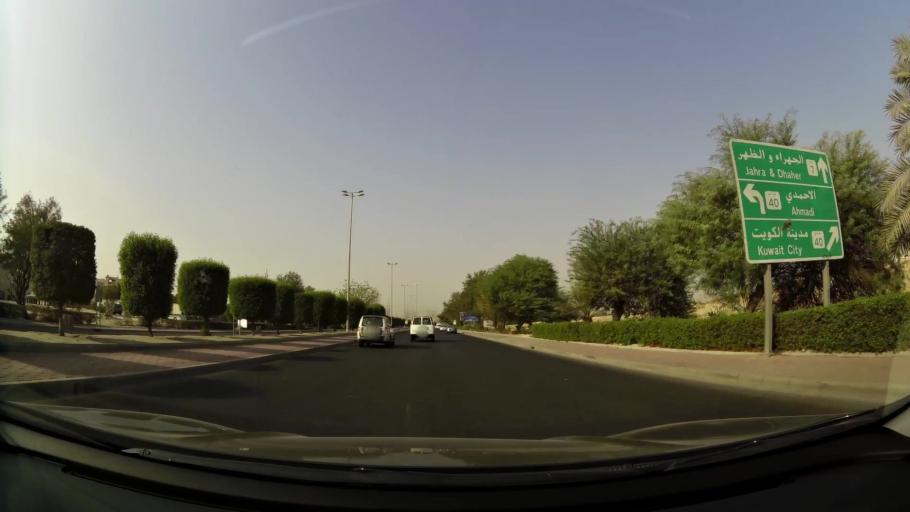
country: KW
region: Mubarak al Kabir
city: Mubarak al Kabir
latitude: 29.1780
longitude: 48.0736
